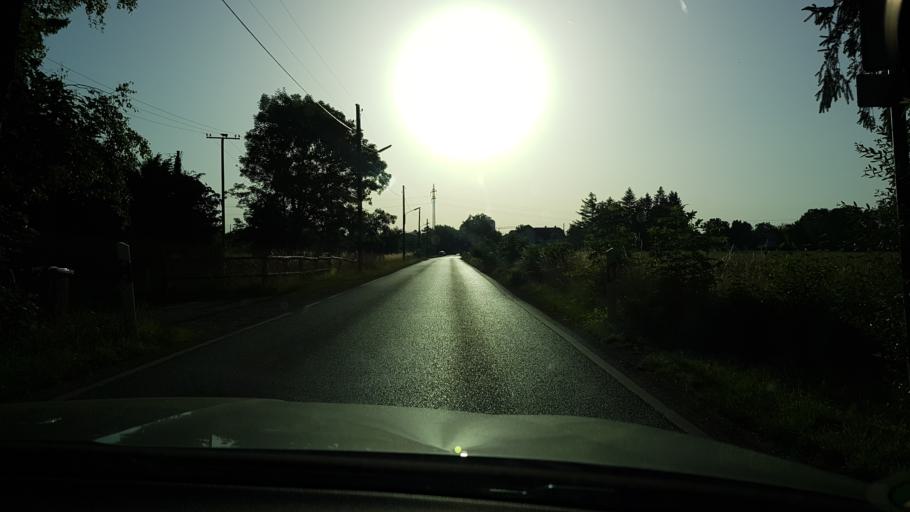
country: DE
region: Bavaria
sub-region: Upper Bavaria
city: Unterfoehring
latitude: 48.1537
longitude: 11.6584
